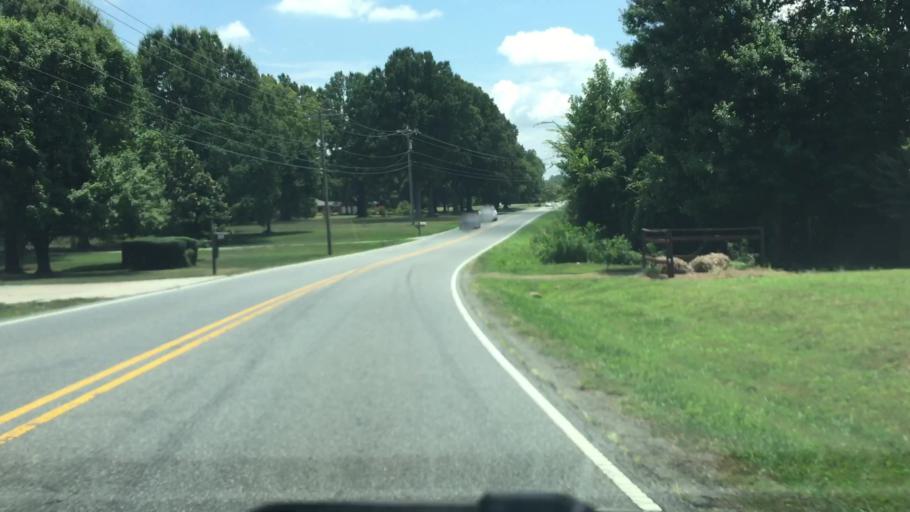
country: US
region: North Carolina
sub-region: Cabarrus County
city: Kannapolis
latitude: 35.4258
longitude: -80.7112
